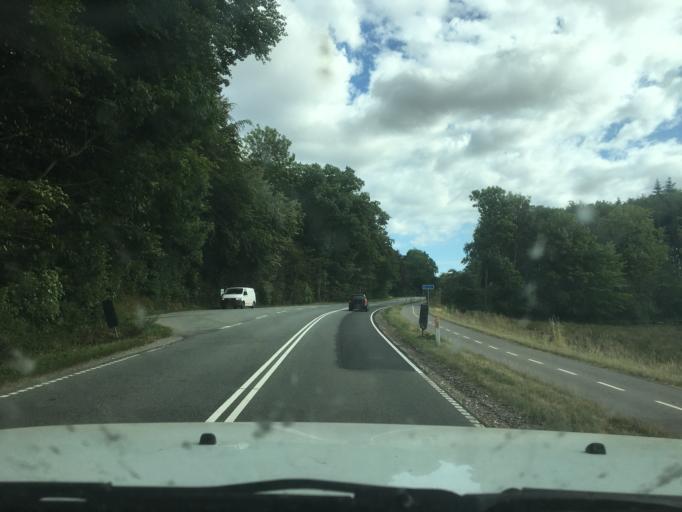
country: DK
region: Central Jutland
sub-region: Syddjurs Kommune
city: Hornslet
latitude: 56.2982
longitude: 10.3169
